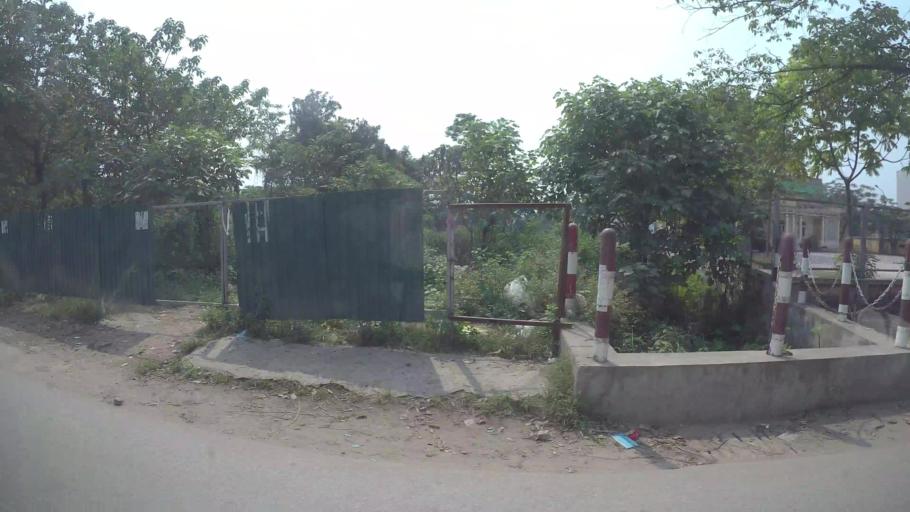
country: VN
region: Ha Noi
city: Ha Dong
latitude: 20.9969
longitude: 105.7562
